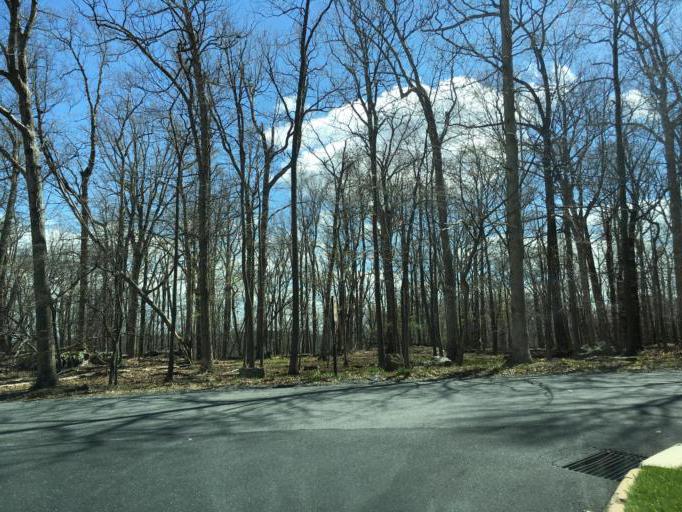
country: US
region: Maryland
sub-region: Frederick County
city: Thurmont
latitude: 39.6421
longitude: -77.4677
